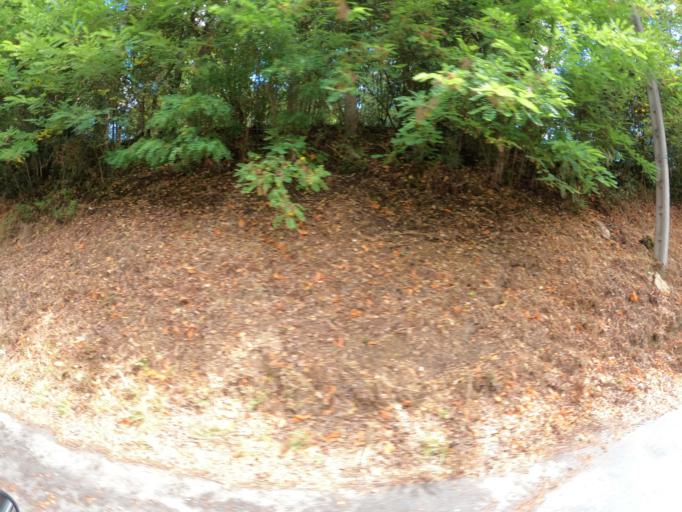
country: FR
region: Pays de la Loire
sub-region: Departement de Maine-et-Loire
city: Avrille
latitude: 47.5316
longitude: -0.6140
